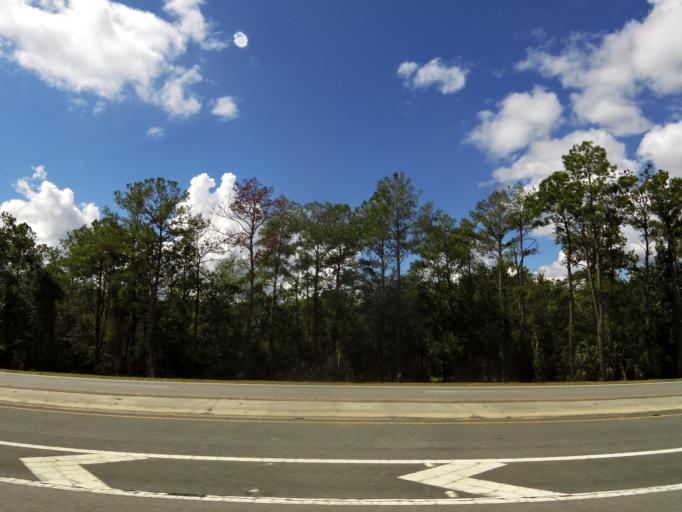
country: US
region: Georgia
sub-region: Charlton County
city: Folkston
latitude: 30.7799
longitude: -81.9788
